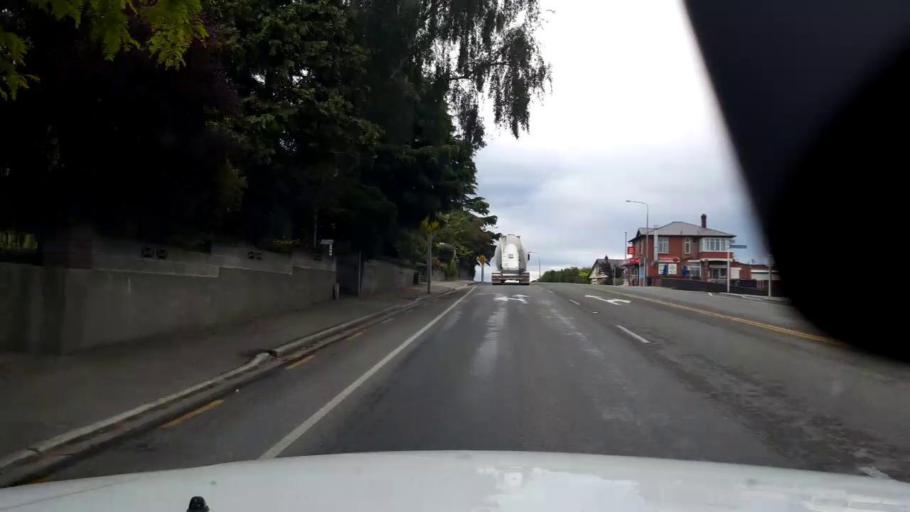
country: NZ
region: Canterbury
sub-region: Timaru District
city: Timaru
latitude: -44.3772
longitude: 171.2422
